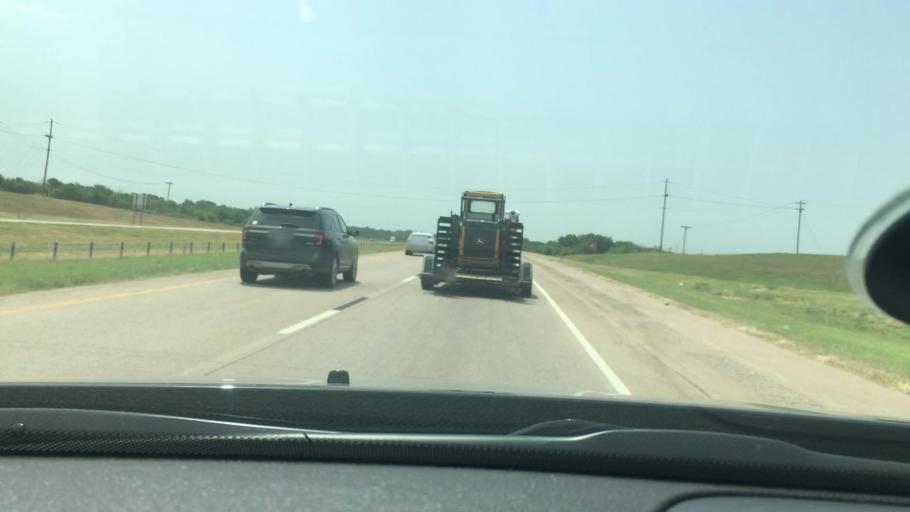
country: US
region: Oklahoma
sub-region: Garvin County
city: Pauls Valley
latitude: 34.7042
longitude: -97.2439
